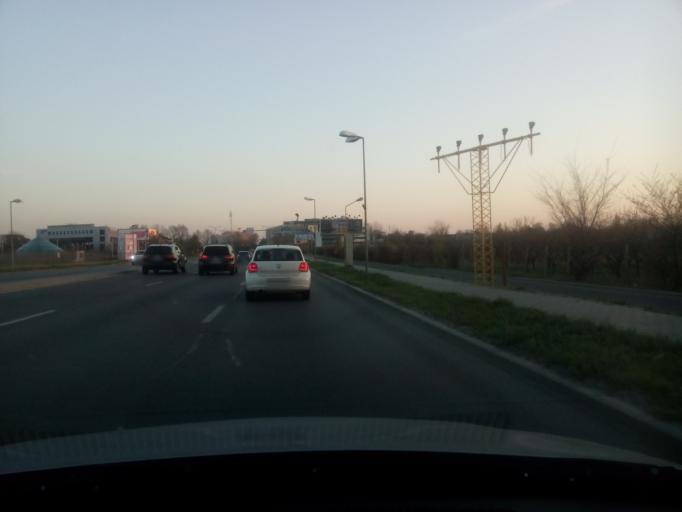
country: RO
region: Ilfov
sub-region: Comuna Otopeni
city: Otopeni
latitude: 44.4987
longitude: 26.0796
